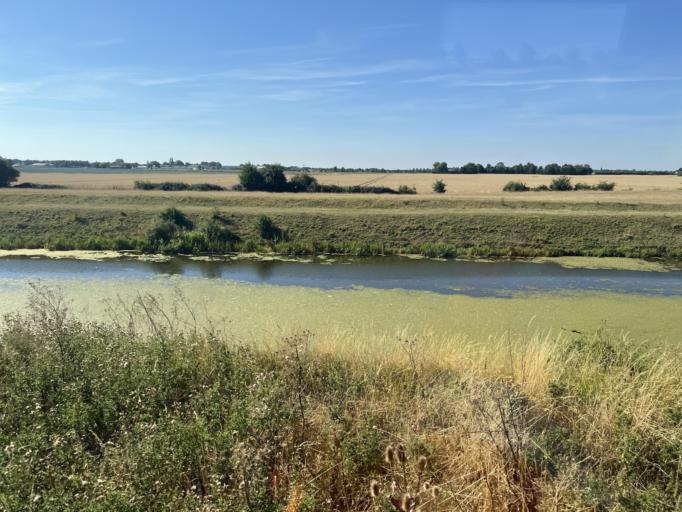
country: GB
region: England
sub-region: Lincolnshire
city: Kirton
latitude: 52.9764
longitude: -0.1278
